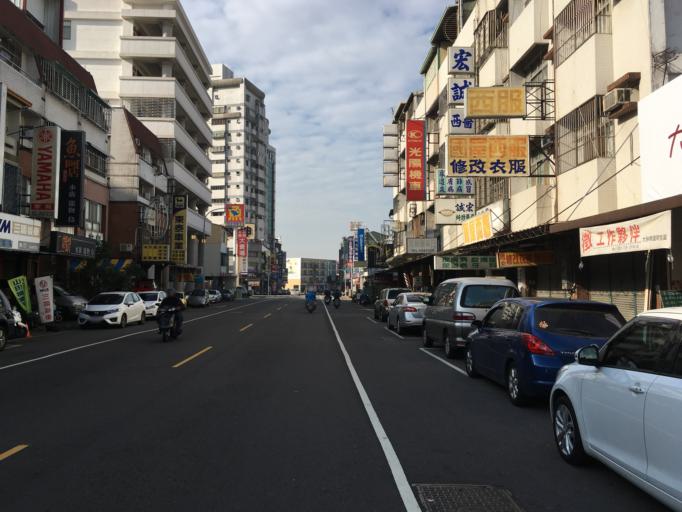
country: TW
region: Taiwan
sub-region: Taichung City
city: Taichung
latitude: 24.1710
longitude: 120.7092
